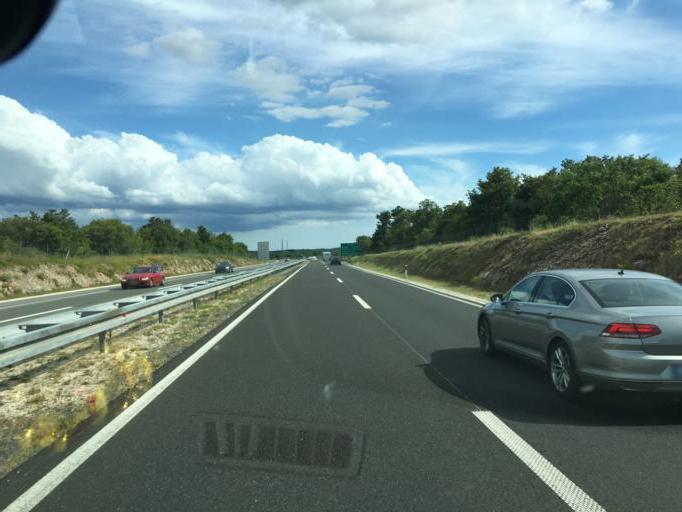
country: HR
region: Istarska
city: Vodnjan
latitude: 45.1052
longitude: 13.8177
